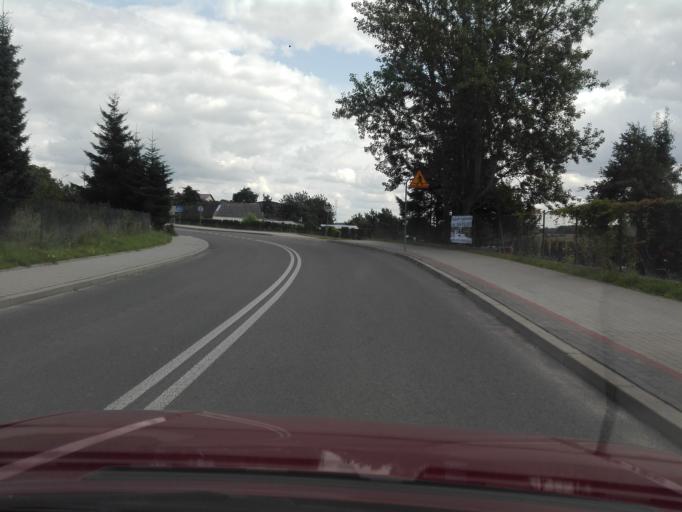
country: PL
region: West Pomeranian Voivodeship
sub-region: Powiat koszalinski
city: Sianow
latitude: 54.2955
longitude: 16.2780
